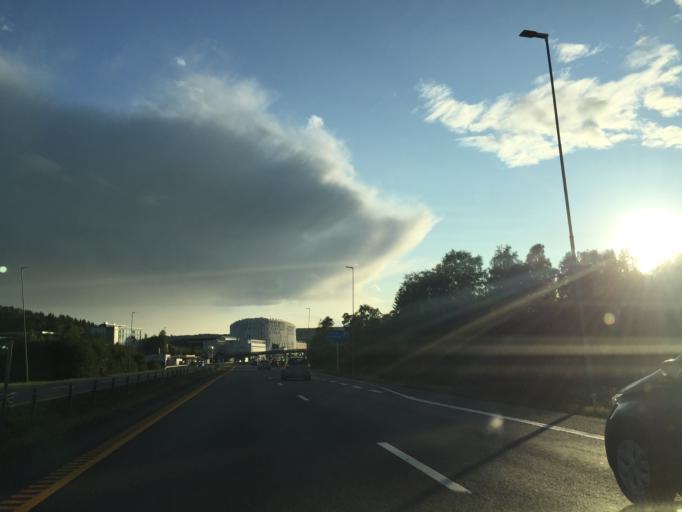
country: NO
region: Akershus
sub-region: Lorenskog
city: Kjenn
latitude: 59.9308
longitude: 10.9726
